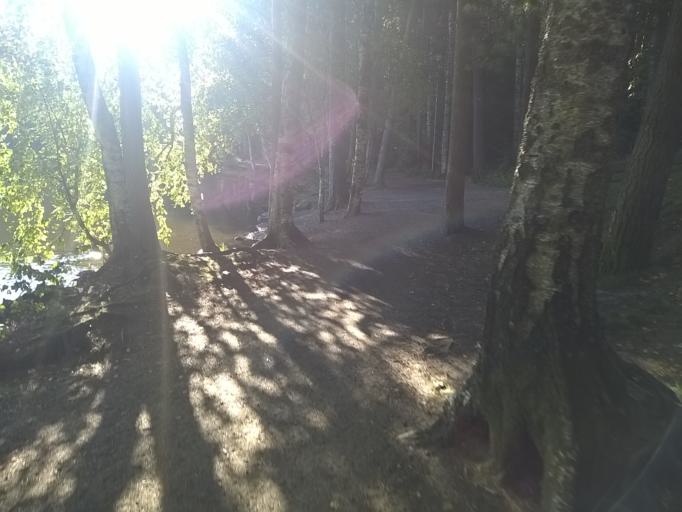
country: FI
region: Pirkanmaa
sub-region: Tampere
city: Tampere
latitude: 61.4473
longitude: 23.8428
